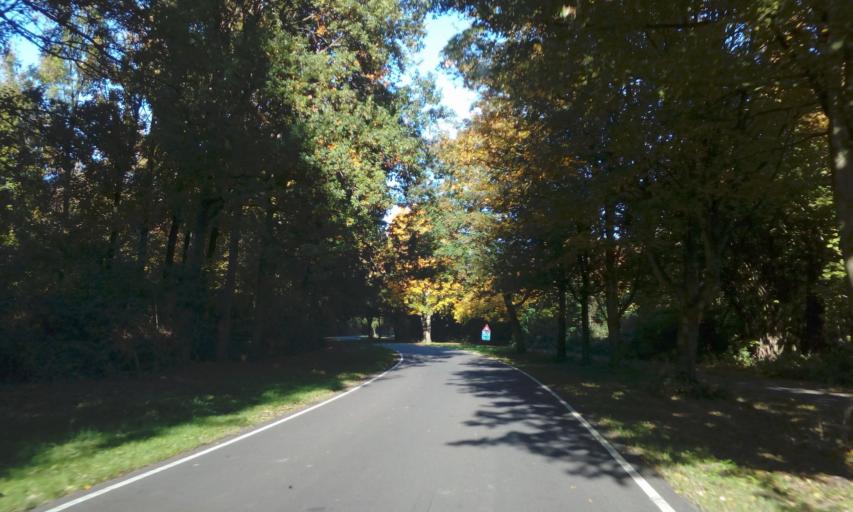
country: NL
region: South Holland
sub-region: Gemeente Lansingerland
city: Bleiswijk
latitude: 52.0033
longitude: 4.5460
